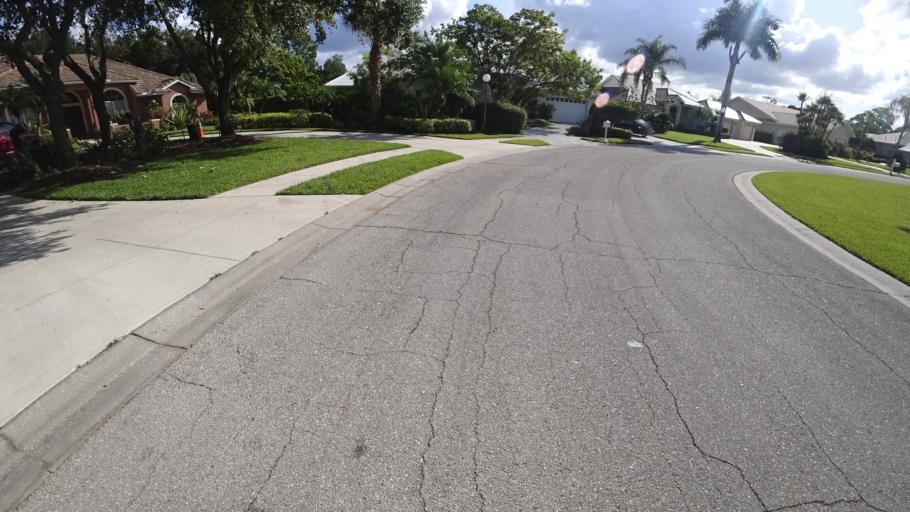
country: US
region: Florida
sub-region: Sarasota County
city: Desoto Lakes
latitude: 27.4094
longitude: -82.4842
